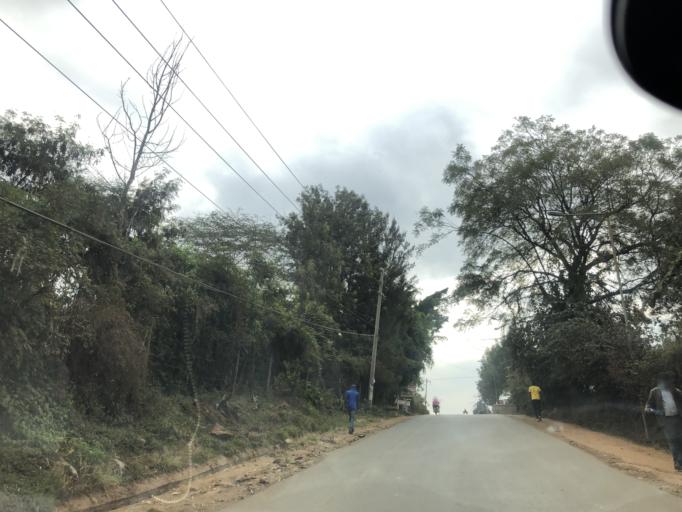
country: KE
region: Kiambu
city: Kiambu
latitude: -1.2121
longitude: 36.8903
